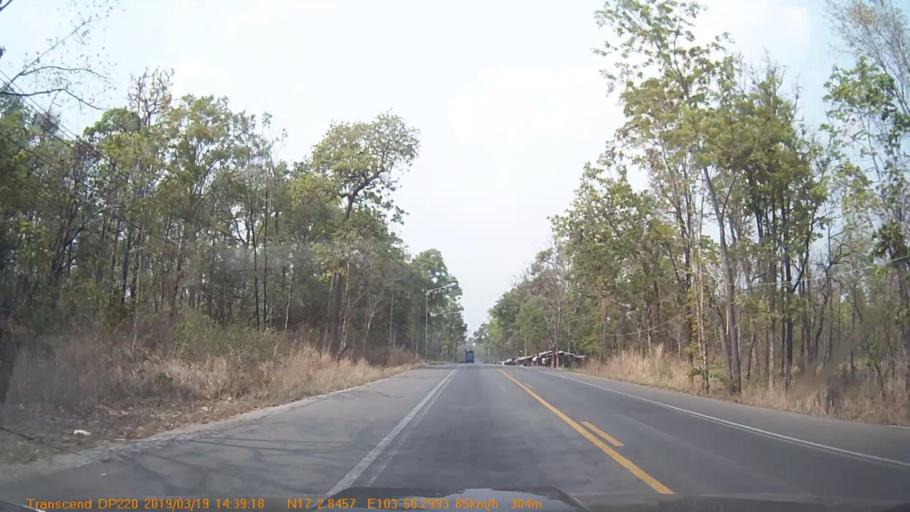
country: TH
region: Sakon Nakhon
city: Phu Phan
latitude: 17.0478
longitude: 103.9716
